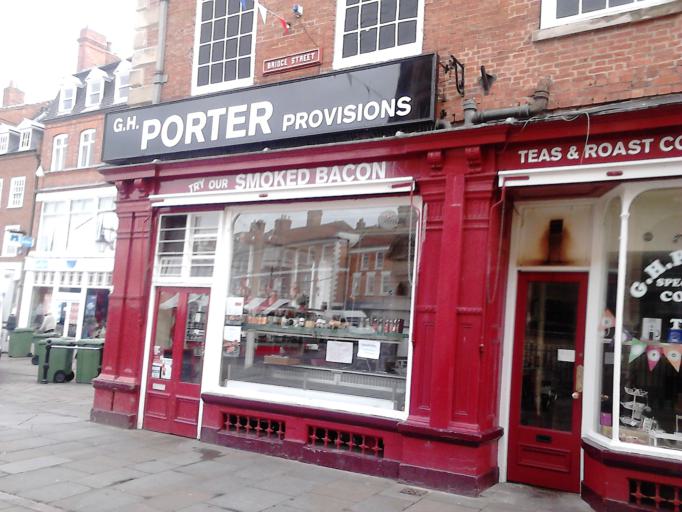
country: GB
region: England
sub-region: Nottinghamshire
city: Newark on Trent
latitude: 53.0761
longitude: -0.8083
